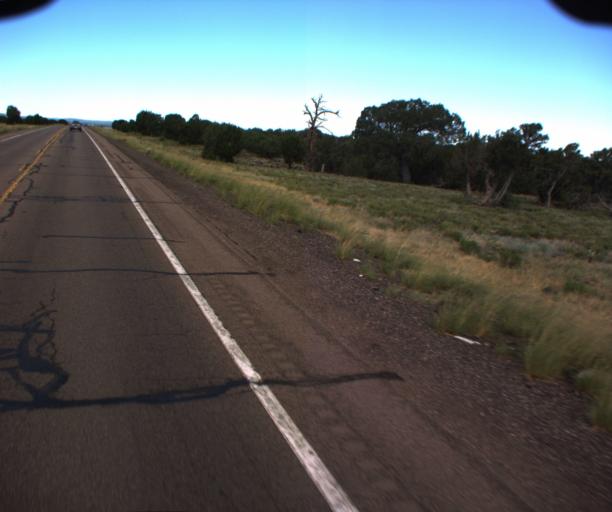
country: US
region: Arizona
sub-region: Navajo County
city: Show Low
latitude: 34.2645
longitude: -109.9596
